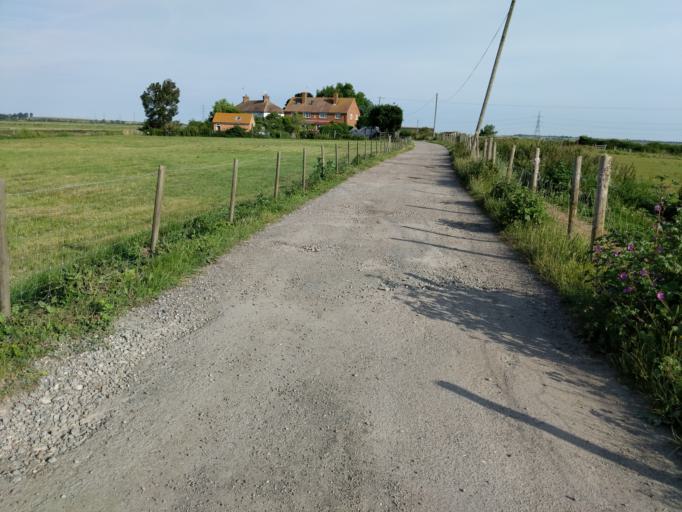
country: GB
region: England
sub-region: Kent
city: Faversham
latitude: 51.3303
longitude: 0.9165
